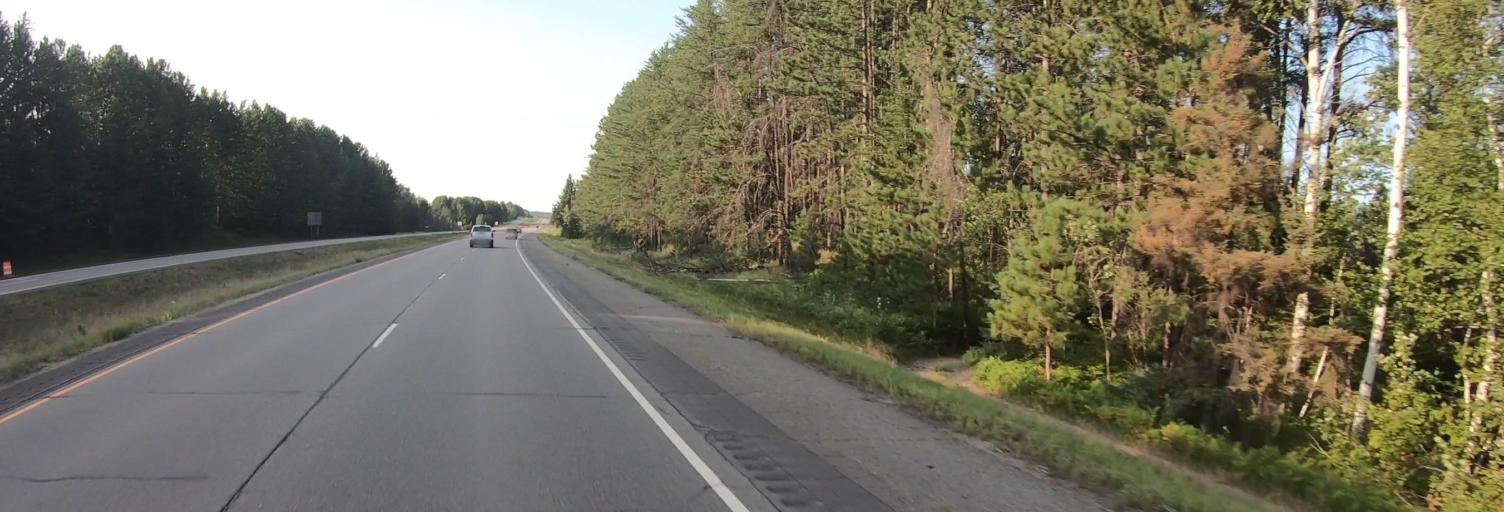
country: US
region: Minnesota
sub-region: Saint Louis County
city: Eveleth
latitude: 47.4066
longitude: -92.5197
